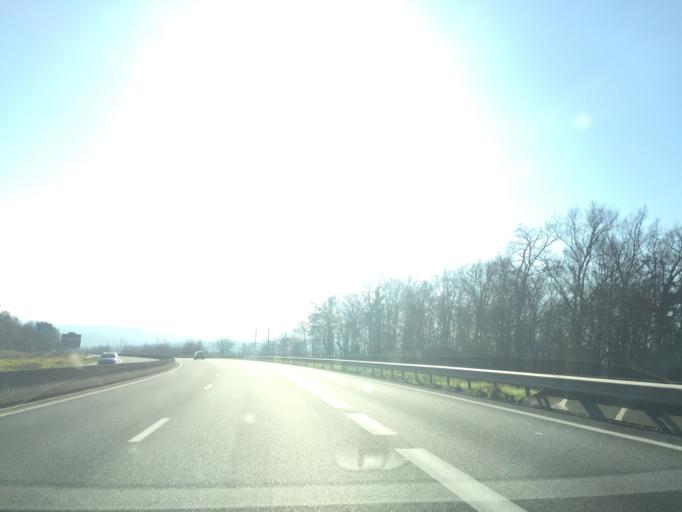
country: FR
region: Limousin
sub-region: Departement de la Correze
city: Donzenac
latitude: 45.2433
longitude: 1.5130
